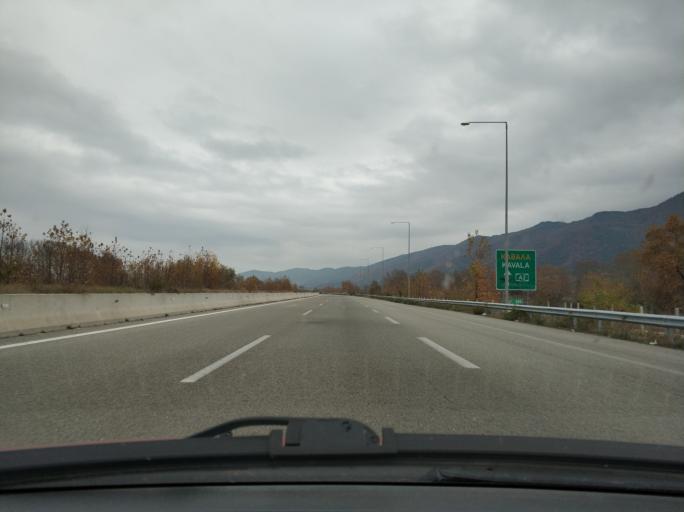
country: GR
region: East Macedonia and Thrace
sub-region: Nomos Kavalas
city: Eleftheres
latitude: 40.8638
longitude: 24.1812
